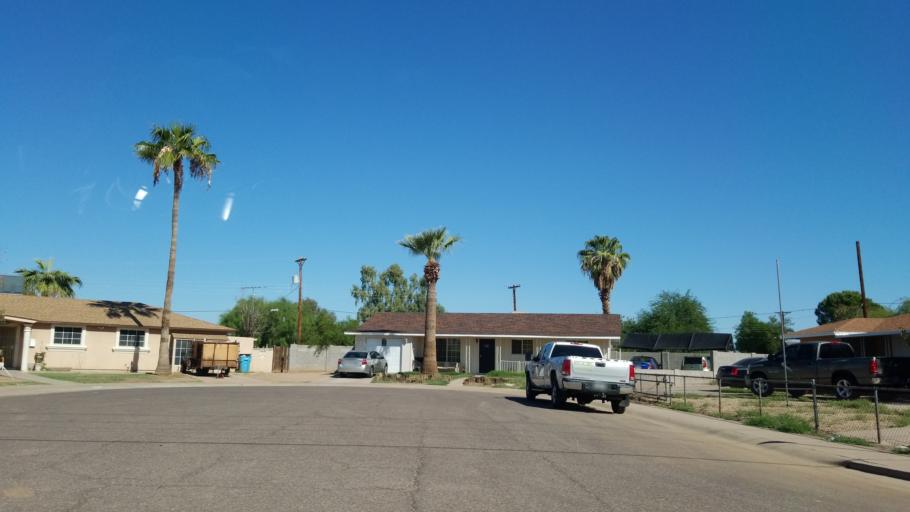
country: US
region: Arizona
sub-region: Maricopa County
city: Glendale
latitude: 33.5023
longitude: -112.1802
